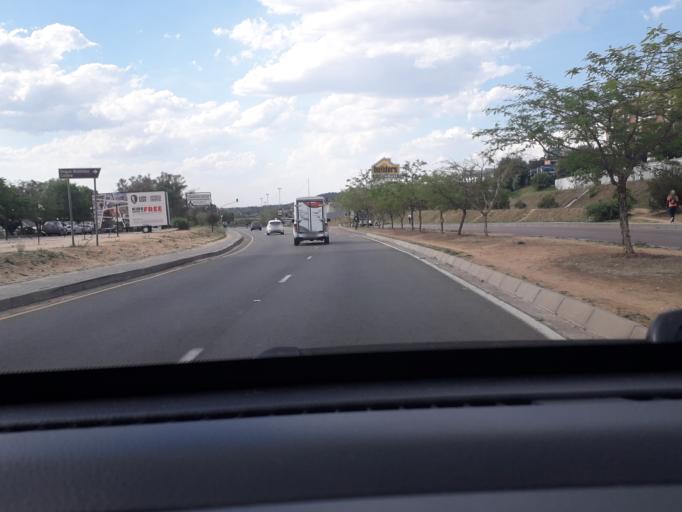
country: ZA
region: Gauteng
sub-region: City of Johannesburg Metropolitan Municipality
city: Midrand
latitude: -26.0349
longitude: 28.0613
